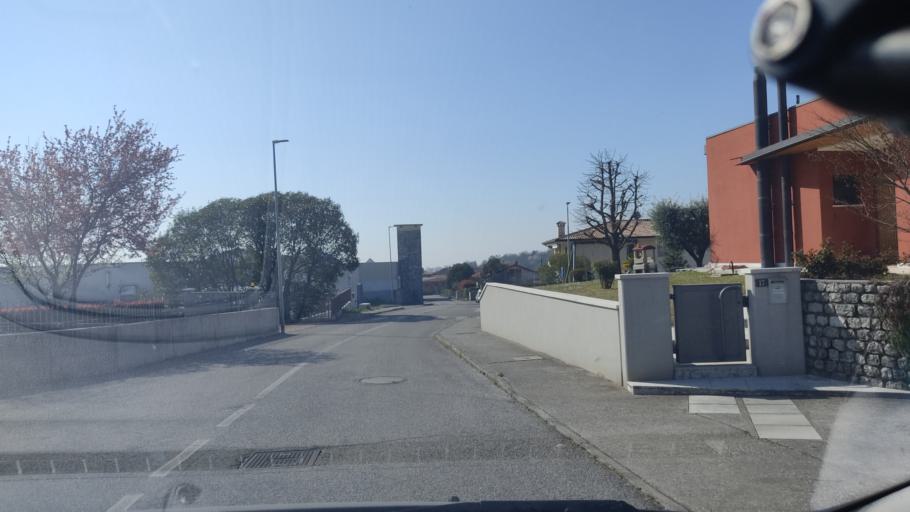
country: IT
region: Friuli Venezia Giulia
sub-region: Provincia di Pordenone
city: Budoia
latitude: 46.0466
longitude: 12.5359
